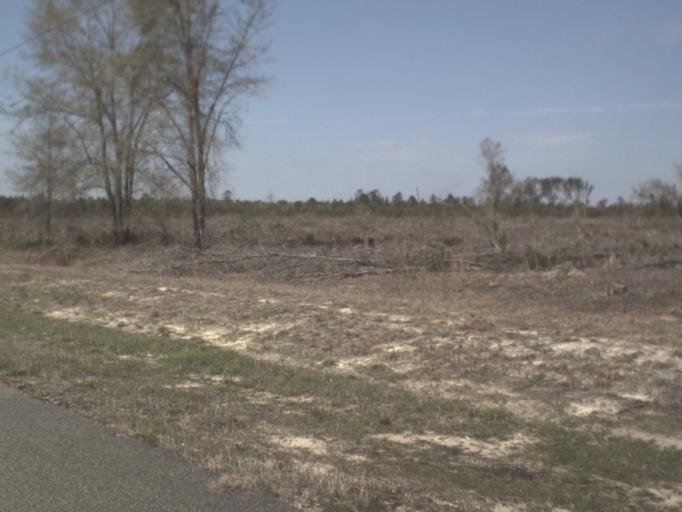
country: US
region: Florida
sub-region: Liberty County
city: Bristol
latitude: 30.5057
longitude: -84.8655
